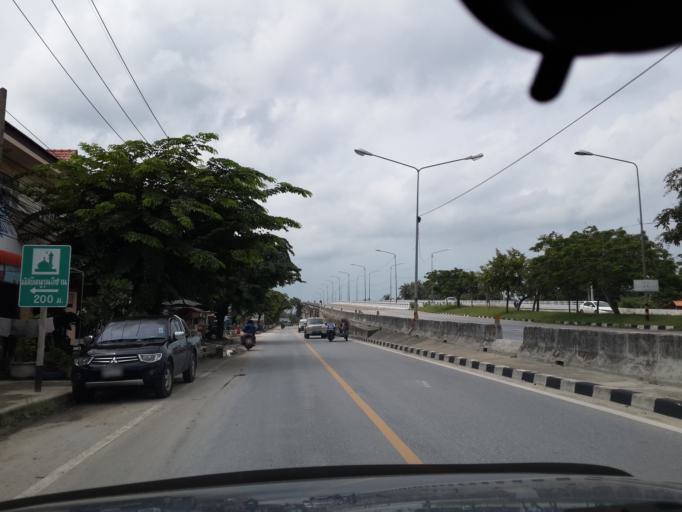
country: TH
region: Pattani
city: Pattani
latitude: 6.8514
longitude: 101.2530
